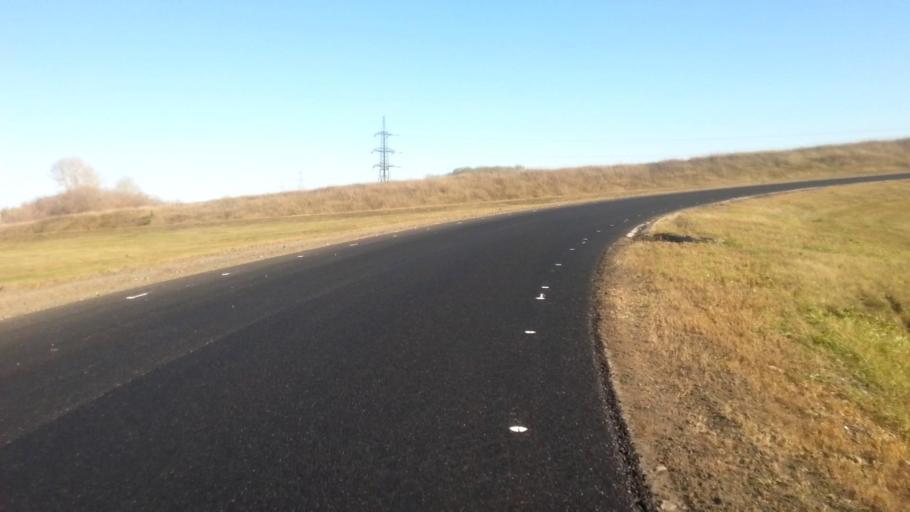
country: RU
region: Altai Krai
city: Novoaltaysk
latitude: 53.3709
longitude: 83.9565
